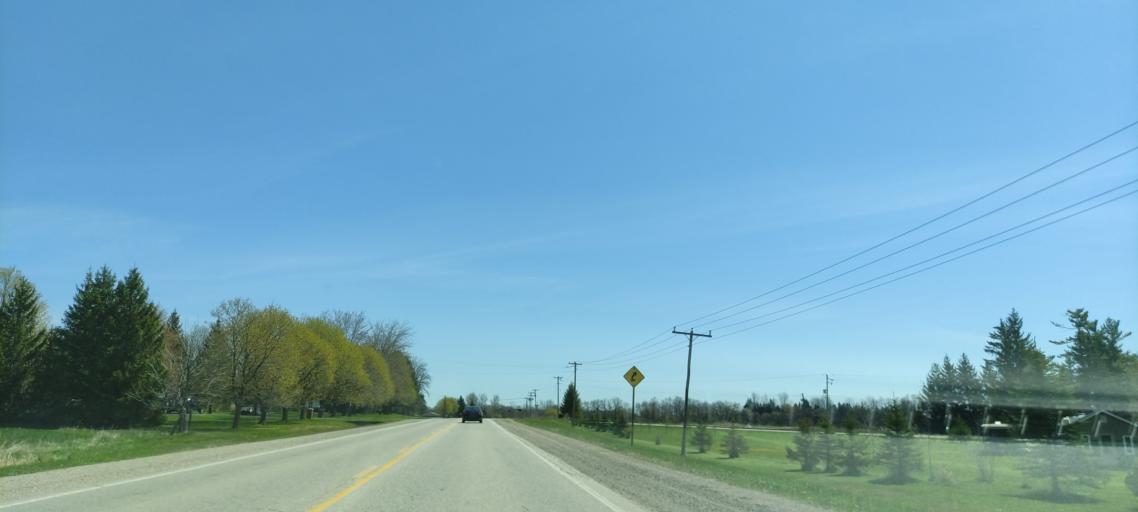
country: CA
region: Ontario
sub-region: Wellington County
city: Guelph
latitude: 43.5755
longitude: -80.3767
